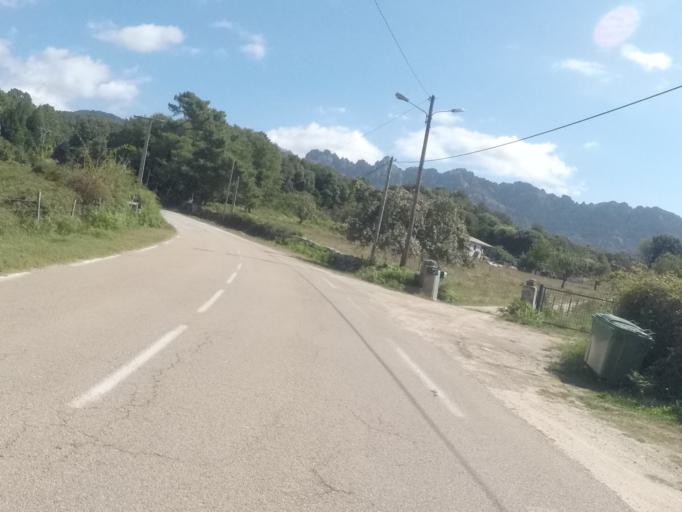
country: FR
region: Corsica
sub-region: Departement de la Corse-du-Sud
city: Zonza
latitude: 41.7588
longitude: 9.1859
